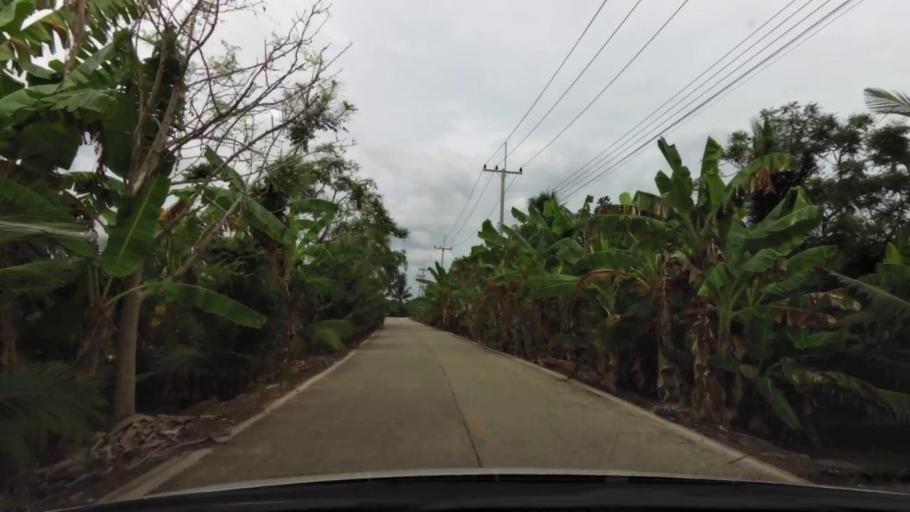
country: TH
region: Ratchaburi
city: Damnoen Saduak
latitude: 13.5685
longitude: 100.0154
